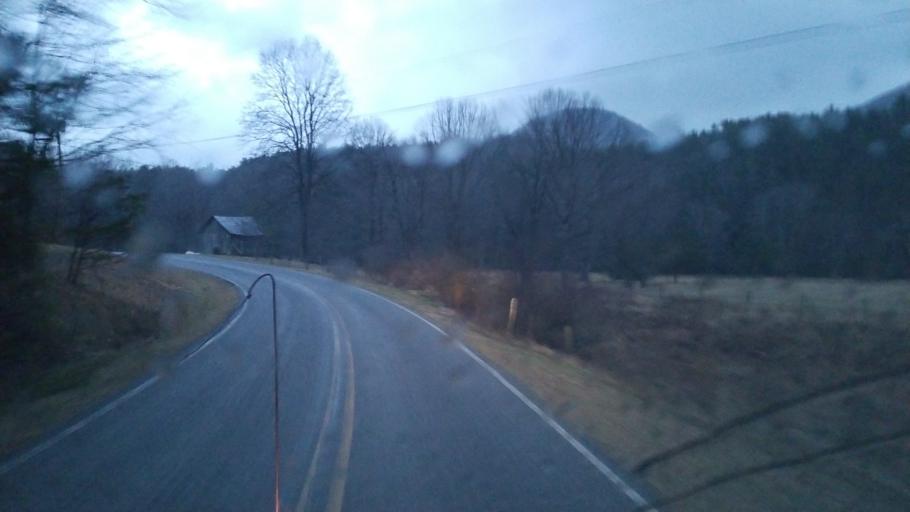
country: US
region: Virginia
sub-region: Pulaski County
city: Pulaski
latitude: 37.1258
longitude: -80.8646
